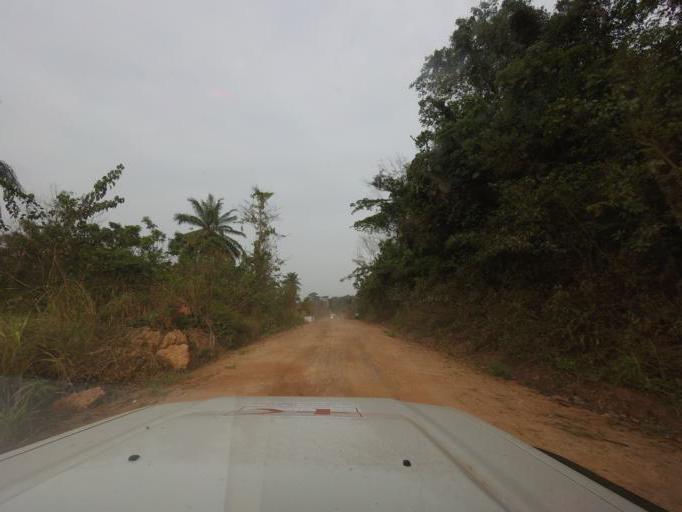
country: LR
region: Lofa
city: Voinjama
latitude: 8.3751
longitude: -9.8607
